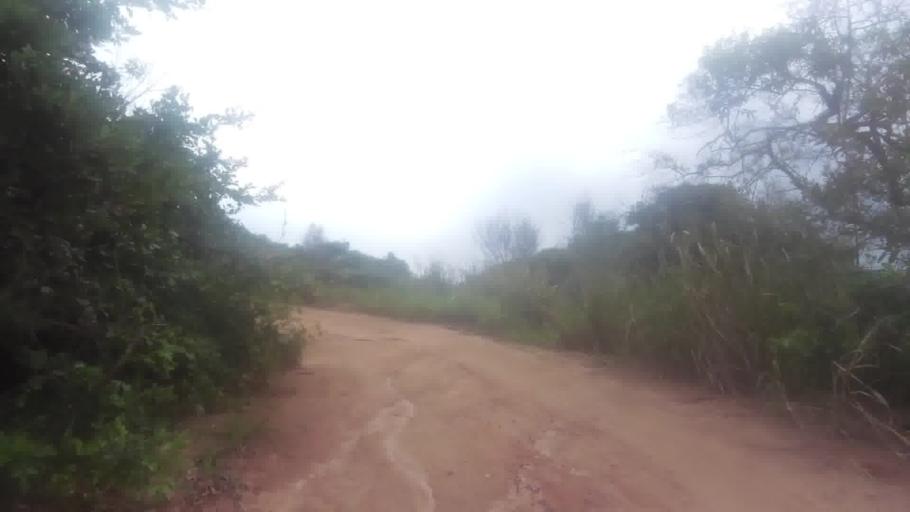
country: BR
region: Espirito Santo
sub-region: Piuma
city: Piuma
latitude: -20.8003
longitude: -40.5843
